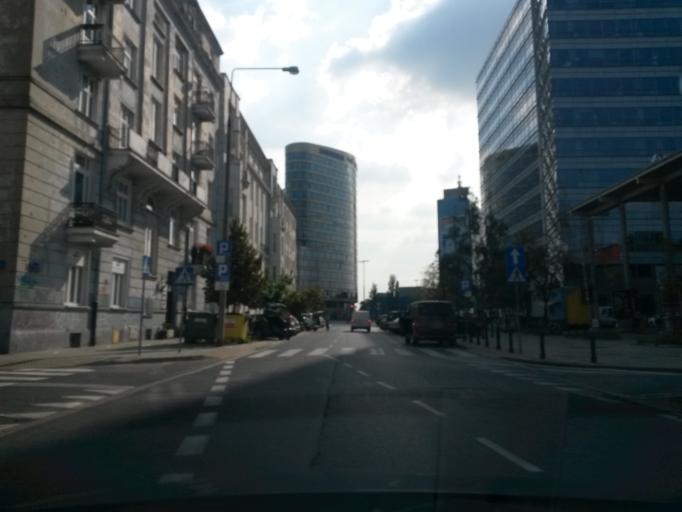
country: PL
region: Masovian Voivodeship
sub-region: Warszawa
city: Srodmiescie
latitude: 52.2189
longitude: 21.0138
